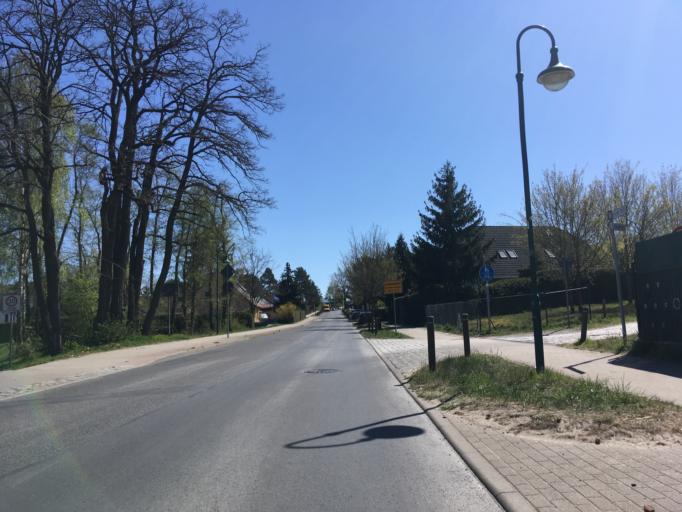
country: DE
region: Brandenburg
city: Bernau bei Berlin
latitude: 52.6457
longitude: 13.5540
